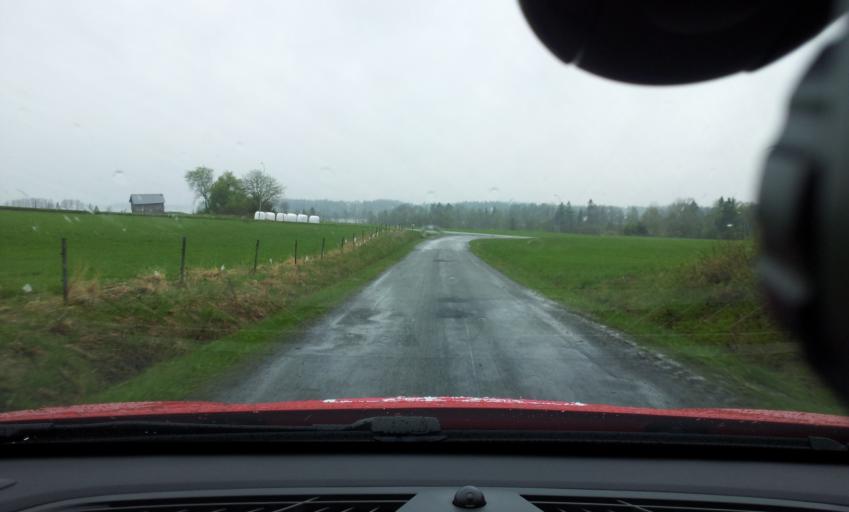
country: SE
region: Jaemtland
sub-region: Bergs Kommun
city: Hoverberg
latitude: 62.9716
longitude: 14.5647
